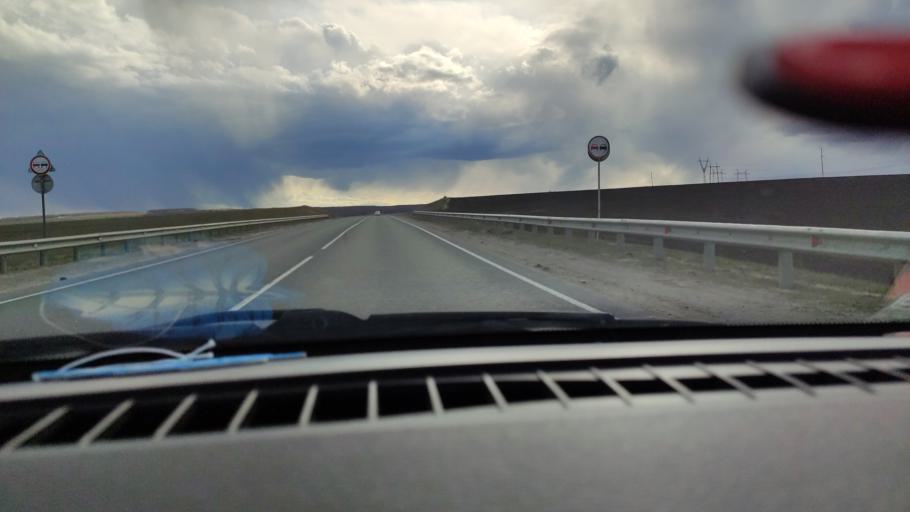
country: RU
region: Saratov
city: Sinodskoye
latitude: 51.9274
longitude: 46.5701
